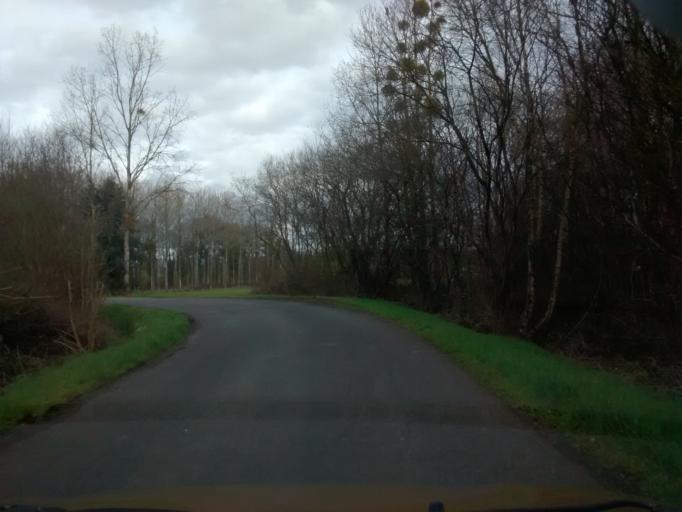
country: FR
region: Brittany
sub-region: Departement des Cotes-d'Armor
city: Merdrignac
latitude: 48.1346
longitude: -2.3836
